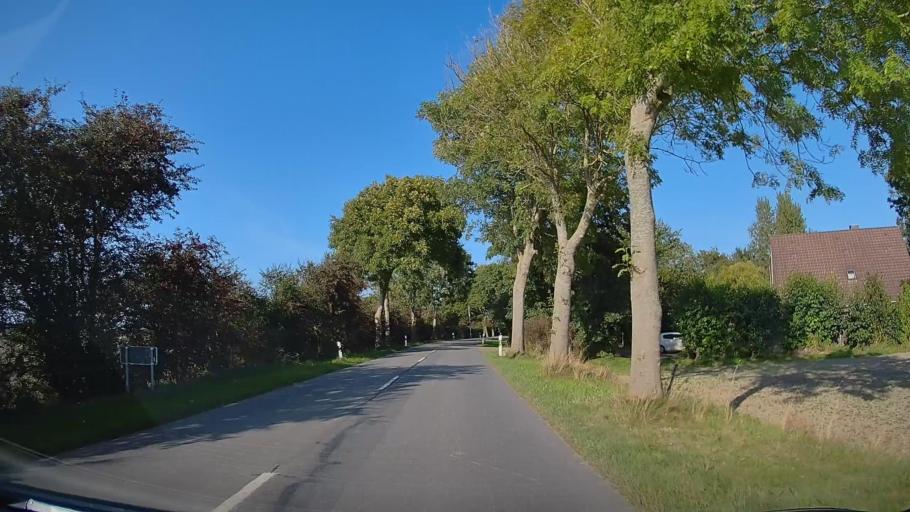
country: DE
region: Lower Saxony
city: Cappel
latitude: 53.7590
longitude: 8.5620
